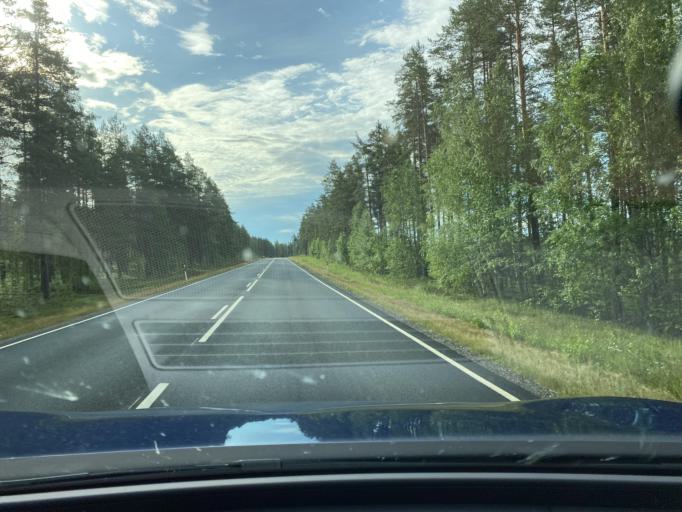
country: FI
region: Central Ostrobothnia
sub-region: Kaustinen
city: Veteli
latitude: 63.4094
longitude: 23.9685
